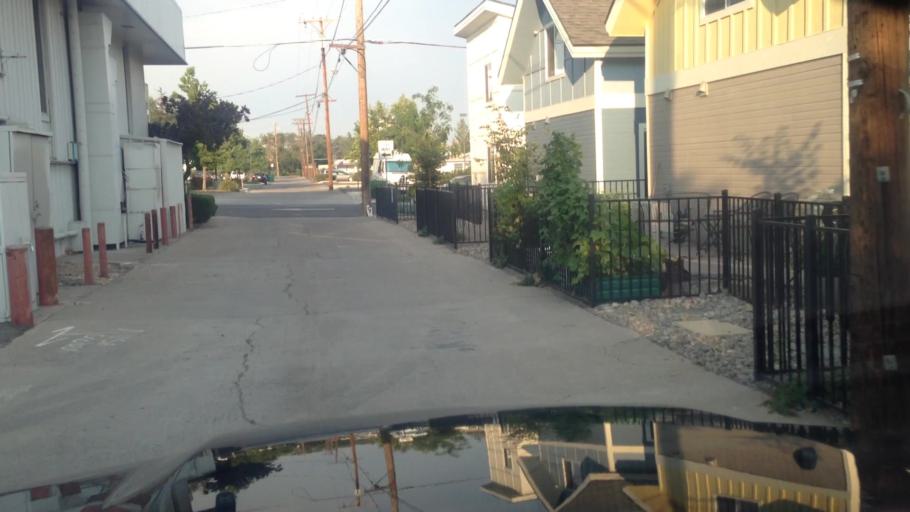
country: US
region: Nevada
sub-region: Washoe County
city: Reno
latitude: 39.5243
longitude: -119.8012
